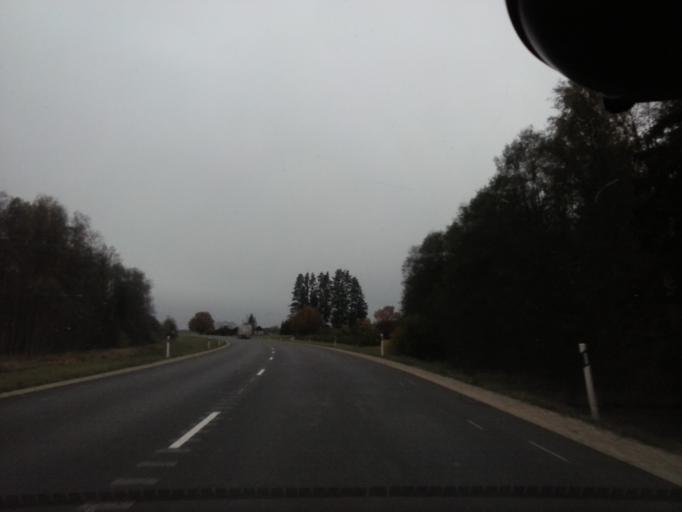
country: EE
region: Jogevamaa
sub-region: Poltsamaa linn
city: Poltsamaa
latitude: 58.7376
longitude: 25.8244
